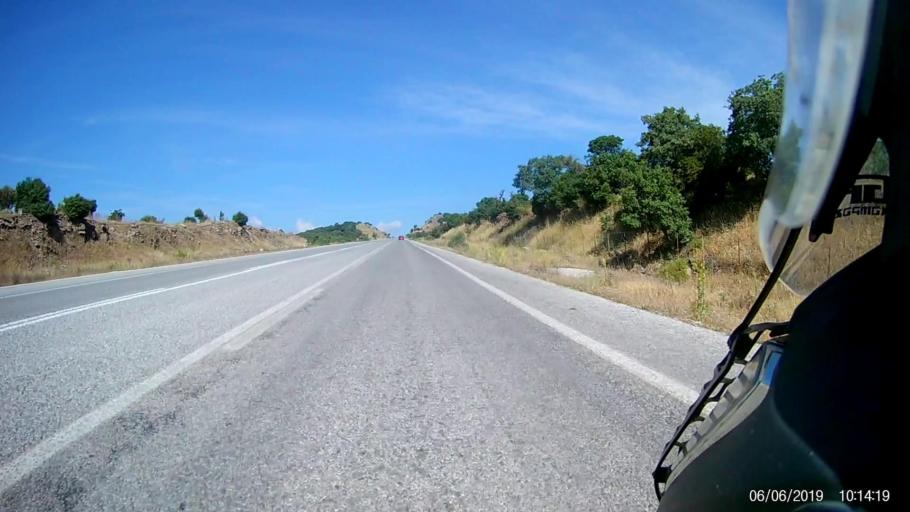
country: TR
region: Canakkale
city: Behram
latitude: 39.5055
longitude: 26.3969
